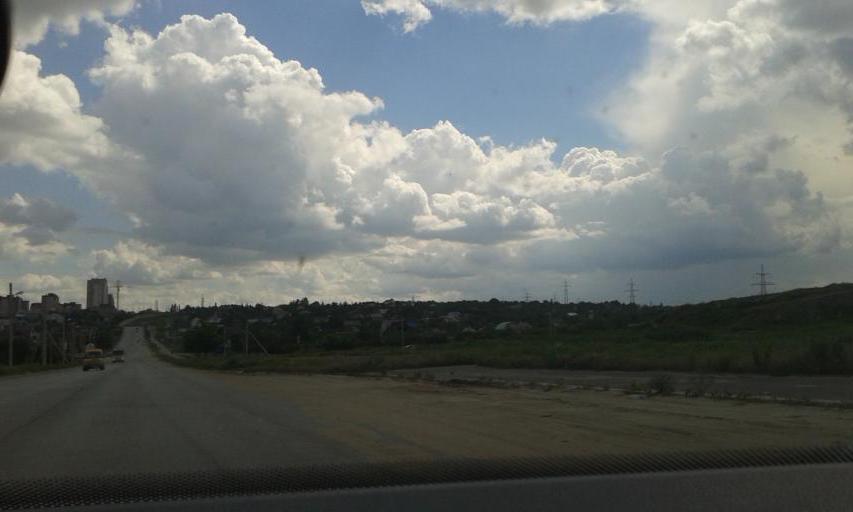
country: RU
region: Volgograd
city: Volgograd
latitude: 48.6573
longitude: 44.4140
